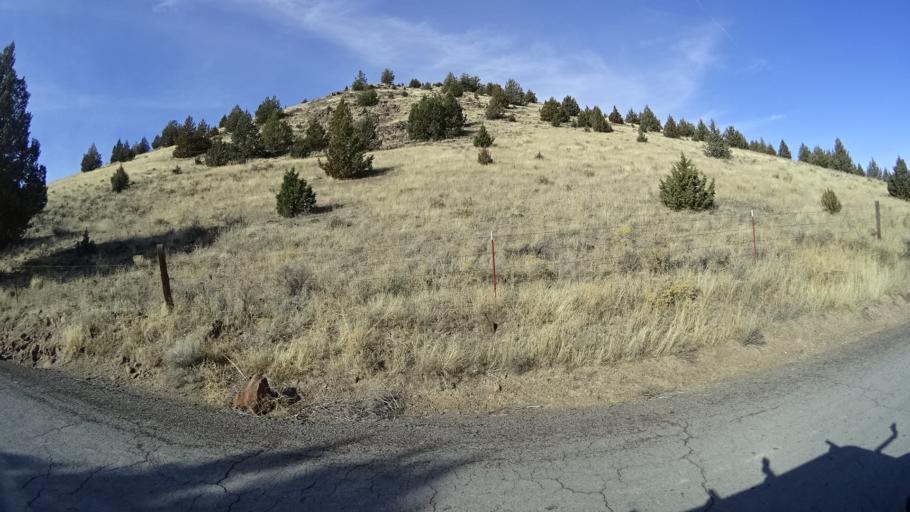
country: US
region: California
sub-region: Siskiyou County
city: Weed
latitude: 41.5567
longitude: -122.4724
